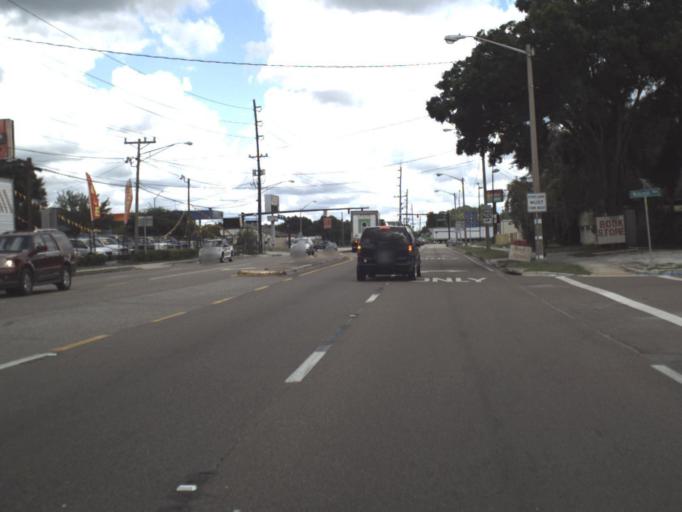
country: US
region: Florida
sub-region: Polk County
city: Winston
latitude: 28.0529
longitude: -81.9901
